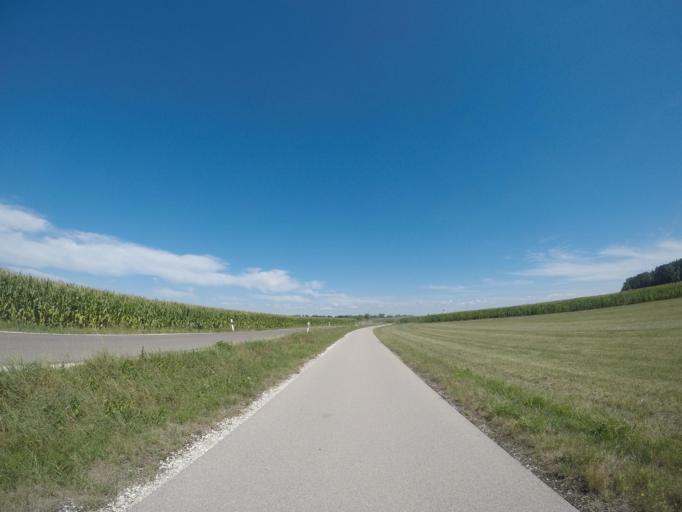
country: DE
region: Bavaria
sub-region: Swabia
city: Holzheim
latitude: 48.3699
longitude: 10.0705
